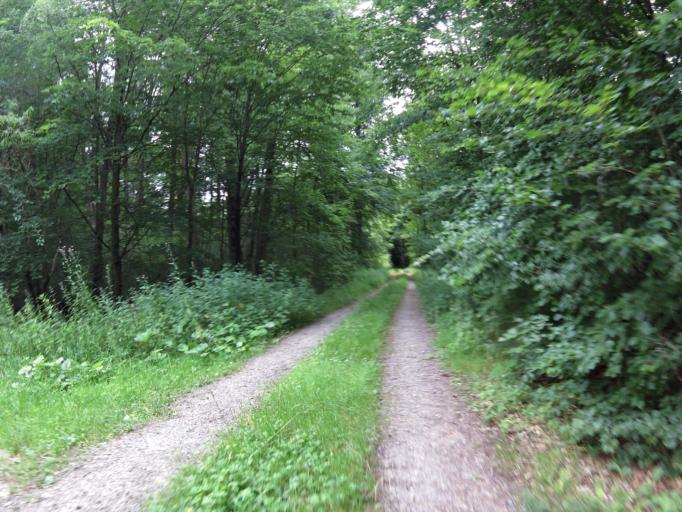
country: DE
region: Bavaria
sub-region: Regierungsbezirk Unterfranken
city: Reichenberg
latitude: 49.7147
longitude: 9.8825
